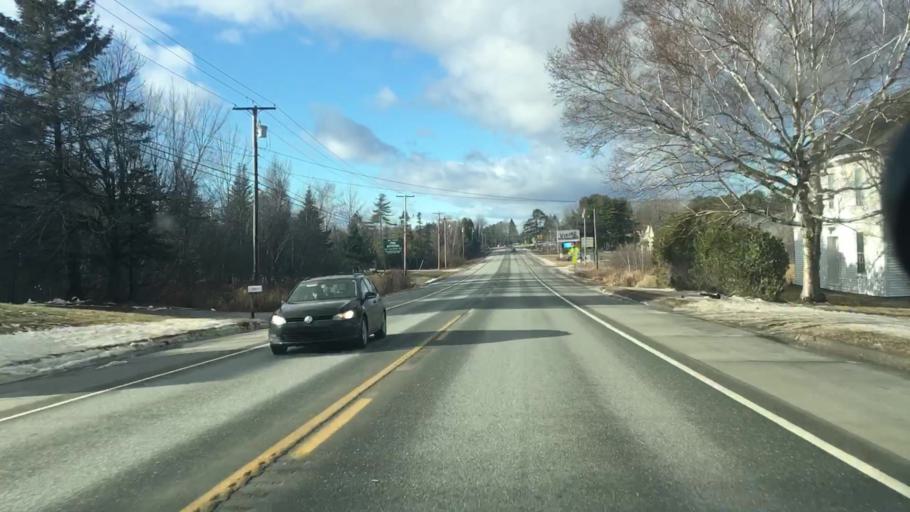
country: US
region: Maine
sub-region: Penobscot County
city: Holden
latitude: 44.7524
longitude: -68.6554
